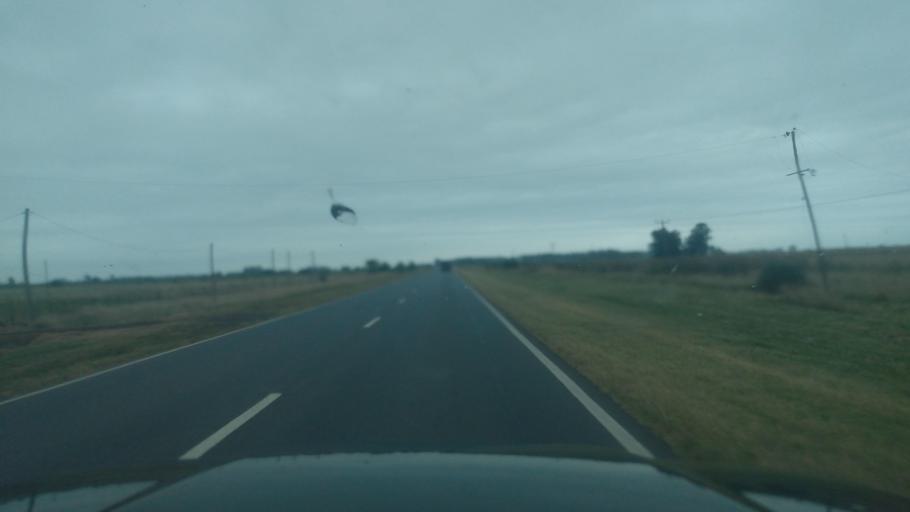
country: AR
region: Buenos Aires
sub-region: Partido de Nueve de Julio
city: Nueve de Julio
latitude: -35.4190
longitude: -60.7862
